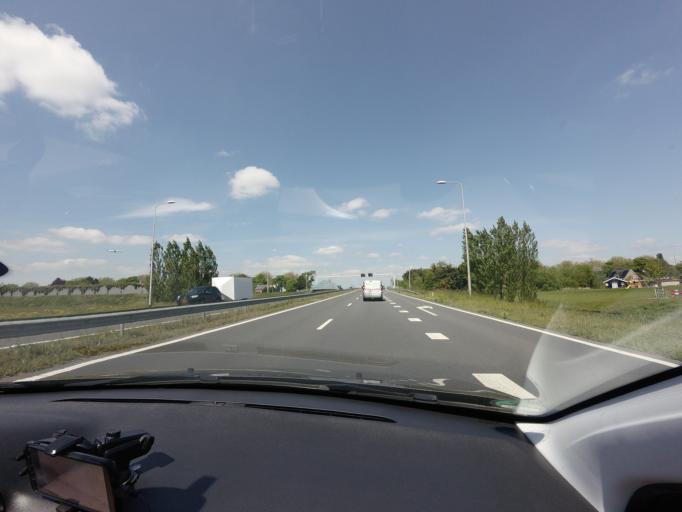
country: NL
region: North Holland
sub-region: Gemeente Aalsmeer
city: Aalsmeer
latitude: 52.2675
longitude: 4.7900
